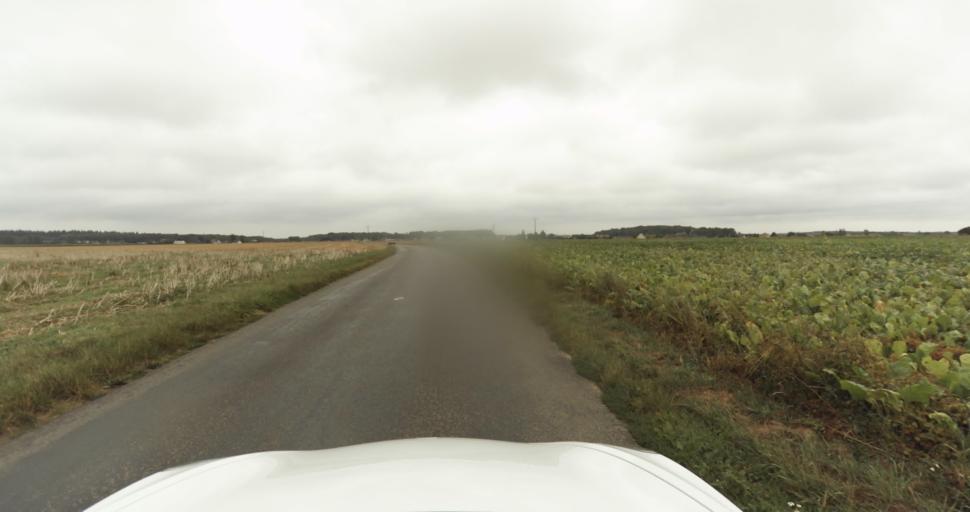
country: FR
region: Haute-Normandie
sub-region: Departement de l'Eure
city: Aviron
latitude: 49.0662
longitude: 1.1181
